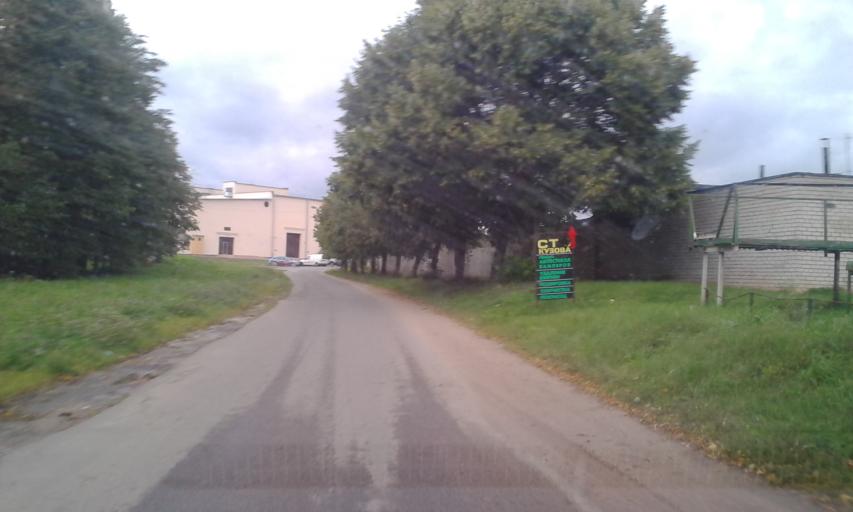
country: BY
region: Minsk
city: Minsk
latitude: 53.9456
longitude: 27.5715
